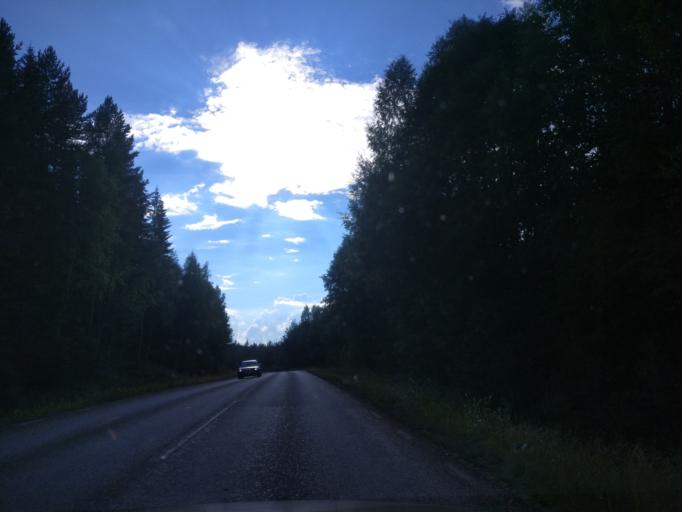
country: SE
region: Dalarna
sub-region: Ludvika Kommun
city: Ludvika
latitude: 60.2870
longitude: 15.1601
